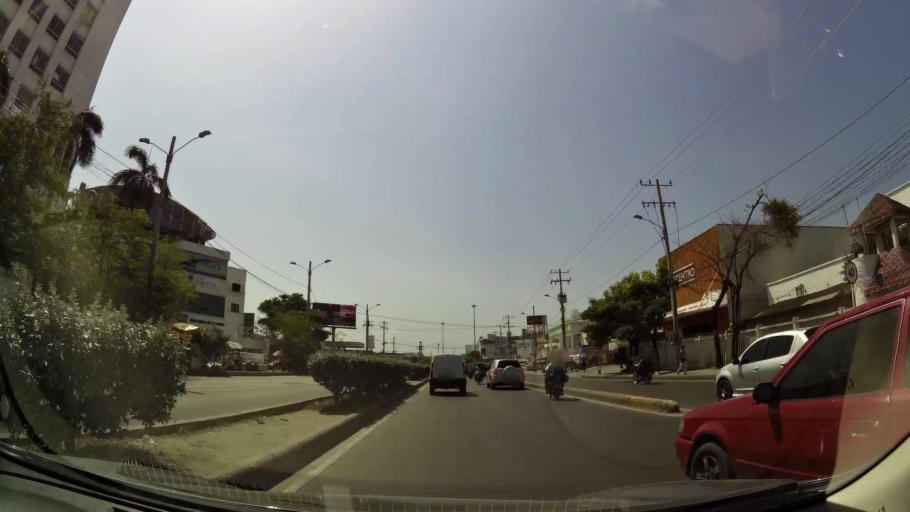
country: CO
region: Bolivar
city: Cartagena
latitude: 10.3940
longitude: -75.4813
